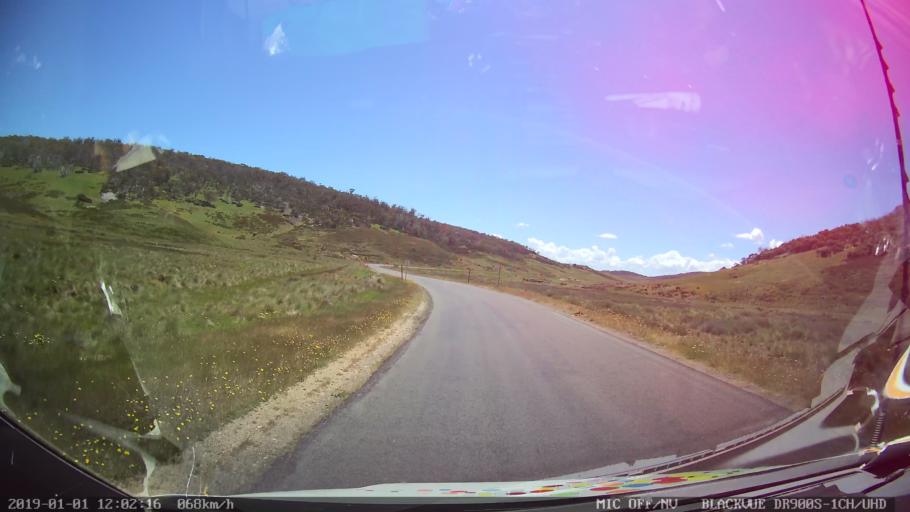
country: AU
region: New South Wales
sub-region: Snowy River
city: Jindabyne
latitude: -35.8738
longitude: 148.4751
